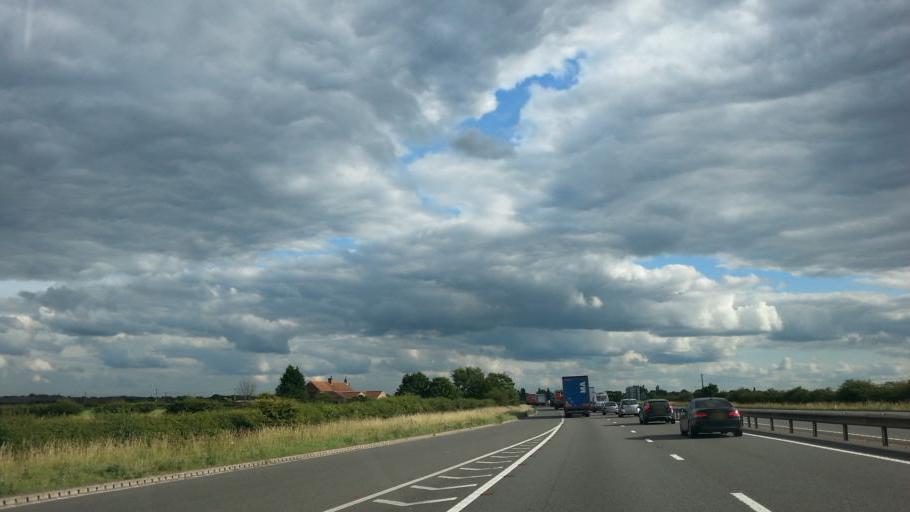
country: GB
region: England
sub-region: Nottinghamshire
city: Newark on Trent
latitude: 53.1168
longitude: -0.8161
